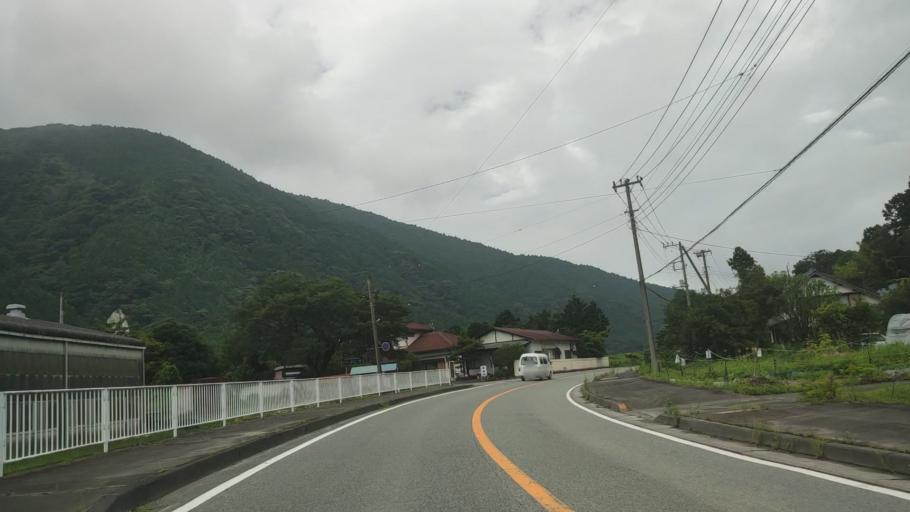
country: JP
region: Shizuoka
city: Fujinomiya
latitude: 35.2113
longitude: 138.5459
